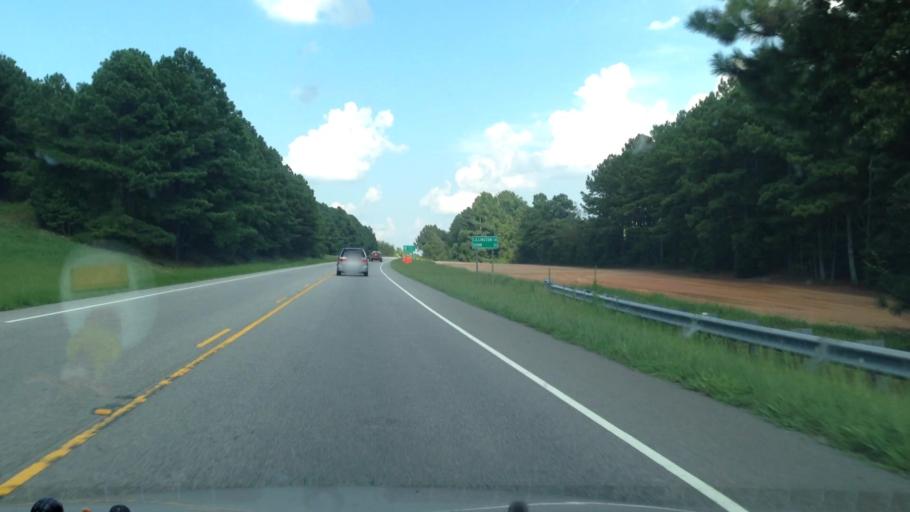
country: US
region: North Carolina
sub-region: Lee County
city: Broadway
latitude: 35.4389
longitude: -79.0495
